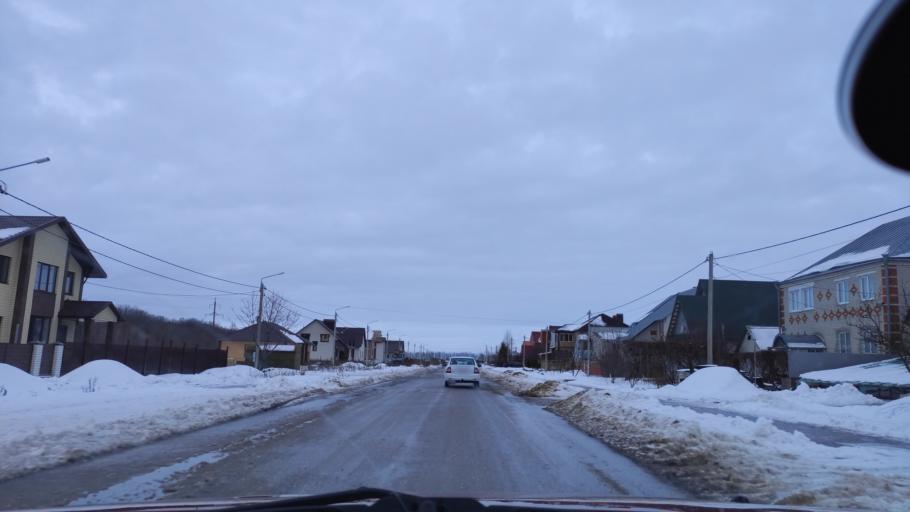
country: RU
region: Tambov
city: Komsomolets
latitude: 52.7597
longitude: 41.3663
